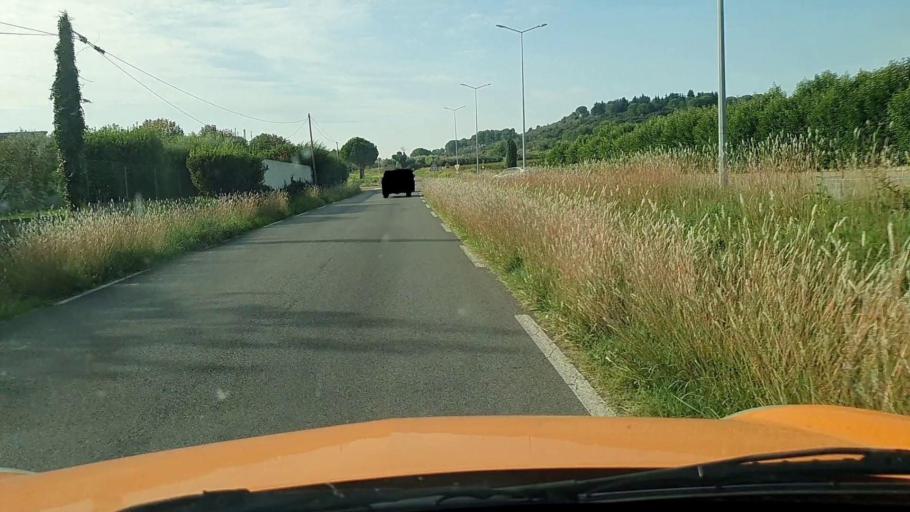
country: FR
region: Languedoc-Roussillon
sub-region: Departement du Gard
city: Generac
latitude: 43.7274
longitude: 4.3430
